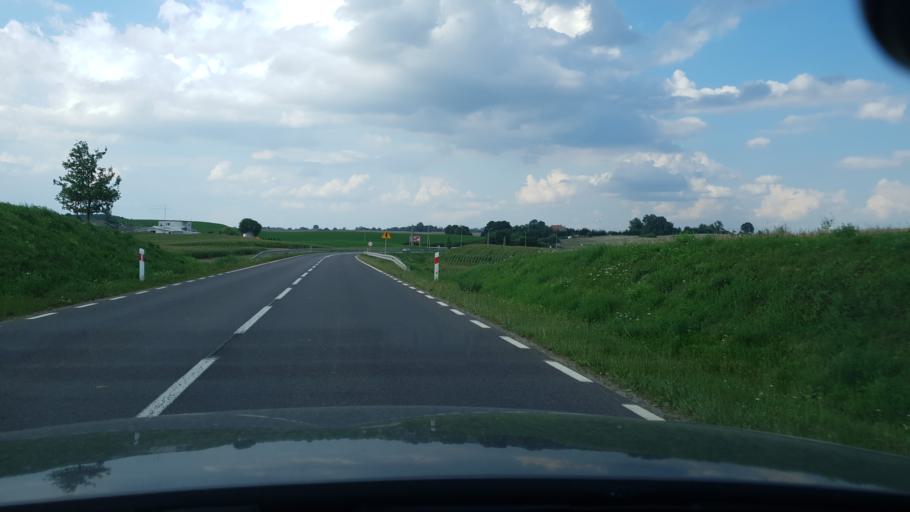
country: PL
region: Kujawsko-Pomorskie
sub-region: Powiat wabrzeski
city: Wabrzezno
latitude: 53.3010
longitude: 18.9268
